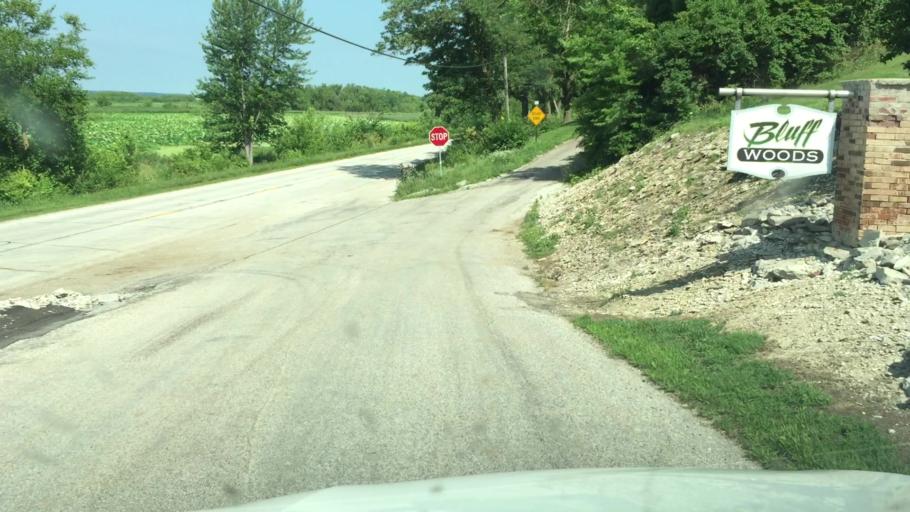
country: US
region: Illinois
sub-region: Hancock County
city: Nauvoo
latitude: 40.5307
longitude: -91.3730
